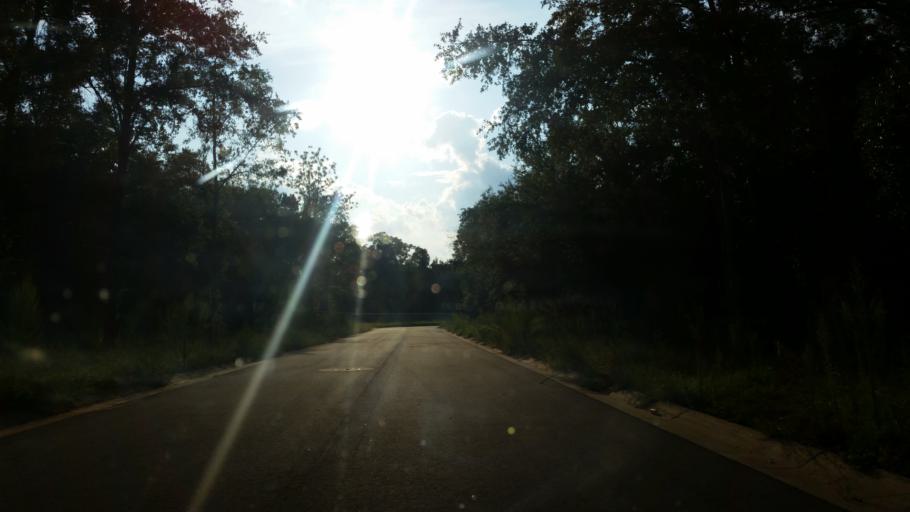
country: US
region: Florida
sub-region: Santa Rosa County
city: Pace
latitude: 30.6148
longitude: -87.1341
